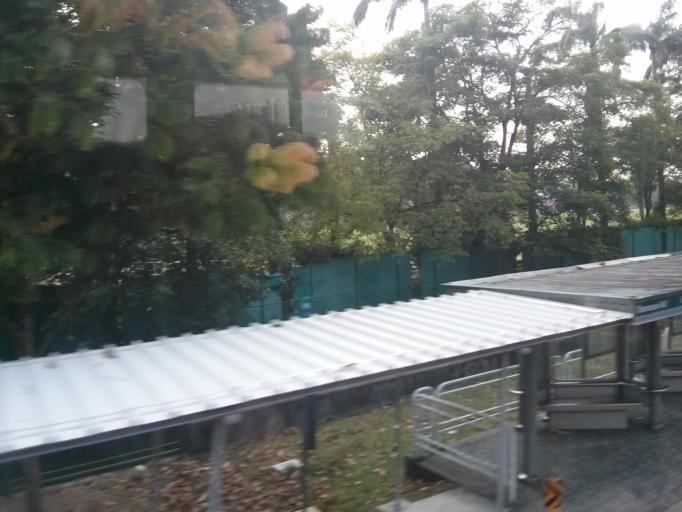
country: SG
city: Singapore
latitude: 1.3316
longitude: 103.8387
